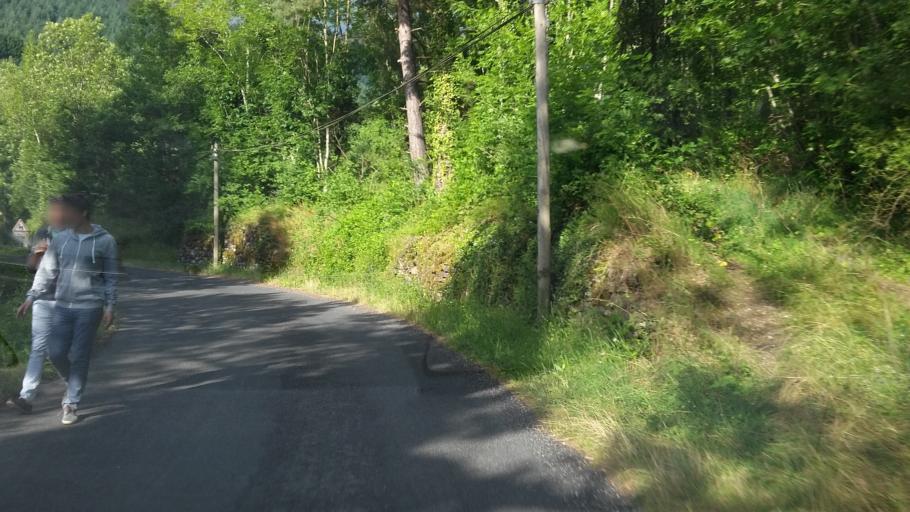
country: FR
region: Languedoc-Roussillon
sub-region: Departement de la Lozere
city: Meyrueis
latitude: 44.0244
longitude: 3.3736
